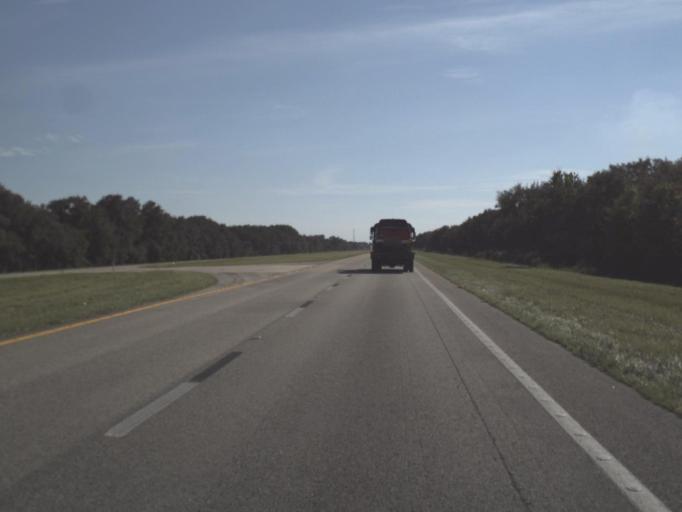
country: US
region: Florida
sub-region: Hendry County
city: Port LaBelle
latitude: 26.9640
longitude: -81.3167
